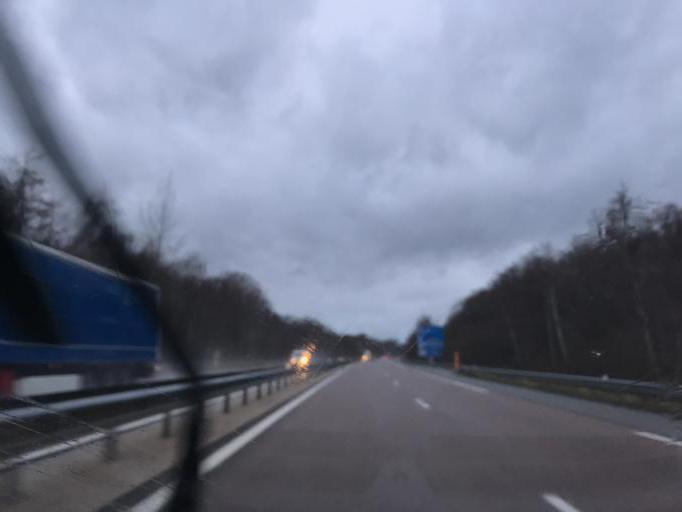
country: FR
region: Franche-Comte
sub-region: Departement du Jura
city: Damparis
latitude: 47.0966
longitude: 5.4043
